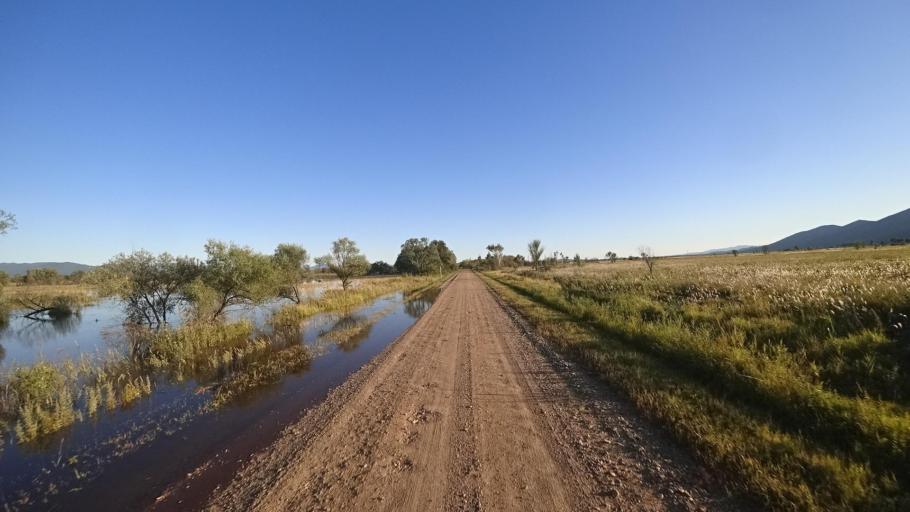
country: RU
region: Primorskiy
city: Kirovskiy
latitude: 44.8120
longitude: 133.6162
